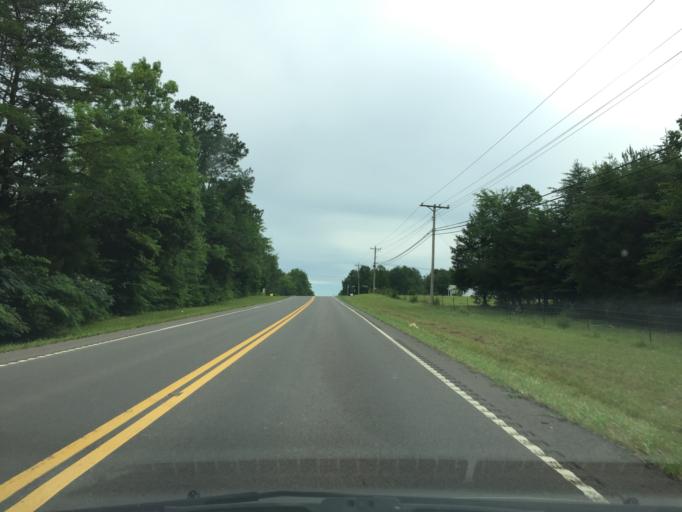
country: US
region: Tennessee
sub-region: Bradley County
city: Hopewell
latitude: 35.3202
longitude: -84.9428
